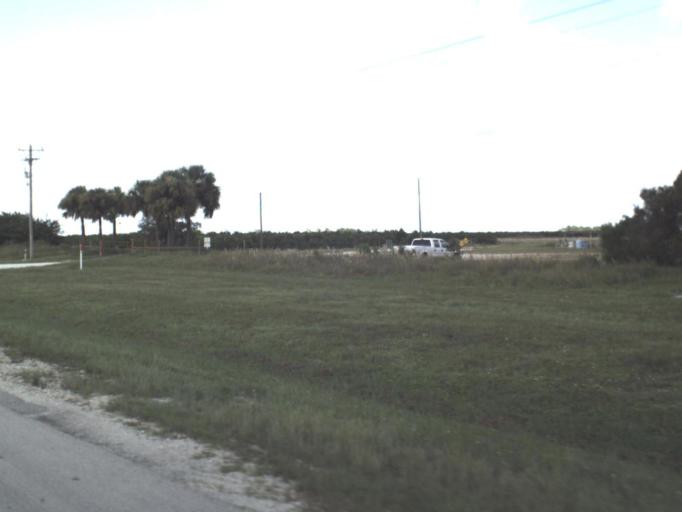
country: US
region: Florida
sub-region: Collier County
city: Immokalee
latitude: 26.4975
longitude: -81.4814
